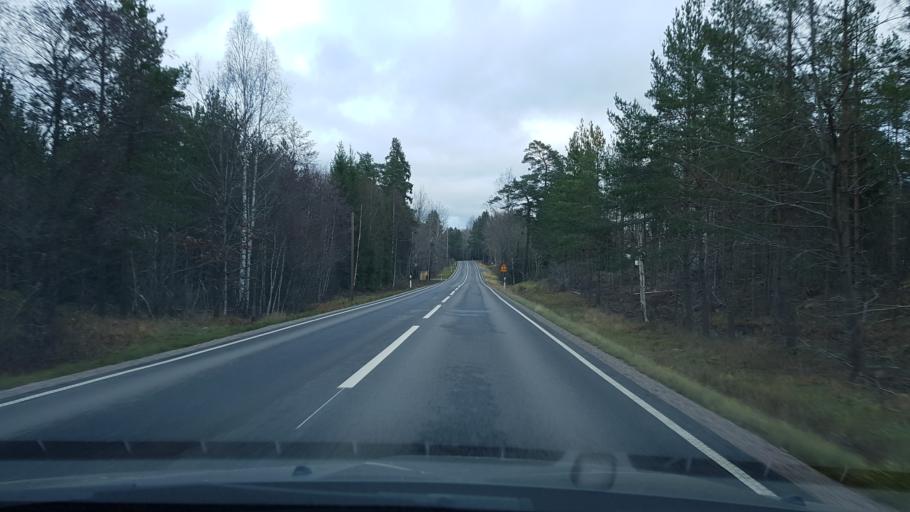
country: SE
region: Stockholm
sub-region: Norrtalje Kommun
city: Skanninge
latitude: 60.0204
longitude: 18.3982
